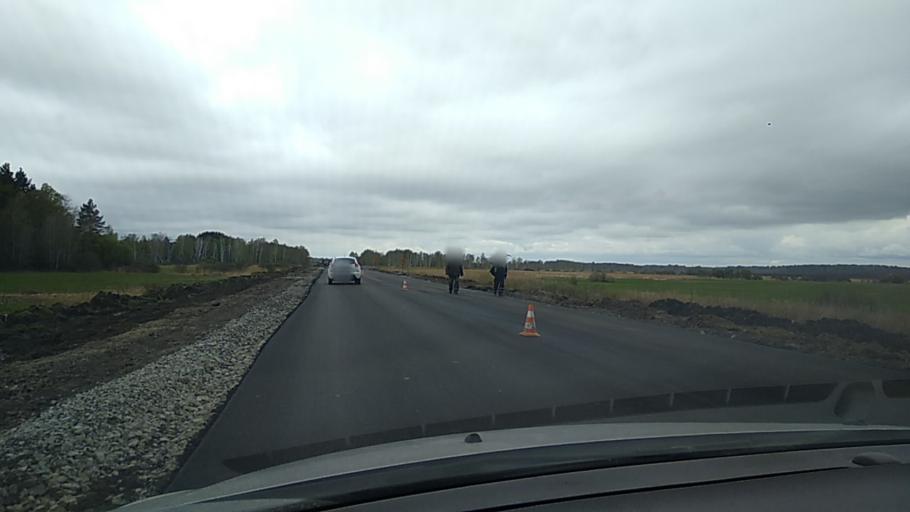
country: RU
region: Kurgan
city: Shadrinsk
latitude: 56.1534
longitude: 63.4159
